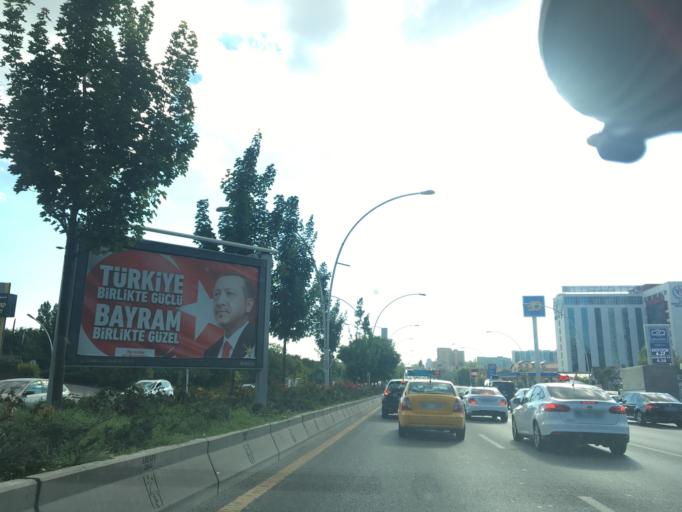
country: TR
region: Ankara
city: Ankara
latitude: 39.9090
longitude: 32.7922
